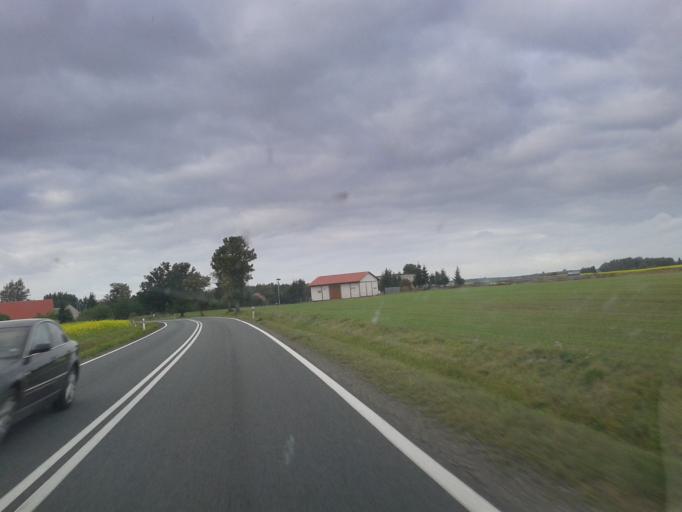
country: PL
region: Kujawsko-Pomorskie
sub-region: Powiat sepolenski
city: Sepolno Krajenskie
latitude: 53.4838
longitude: 17.5198
